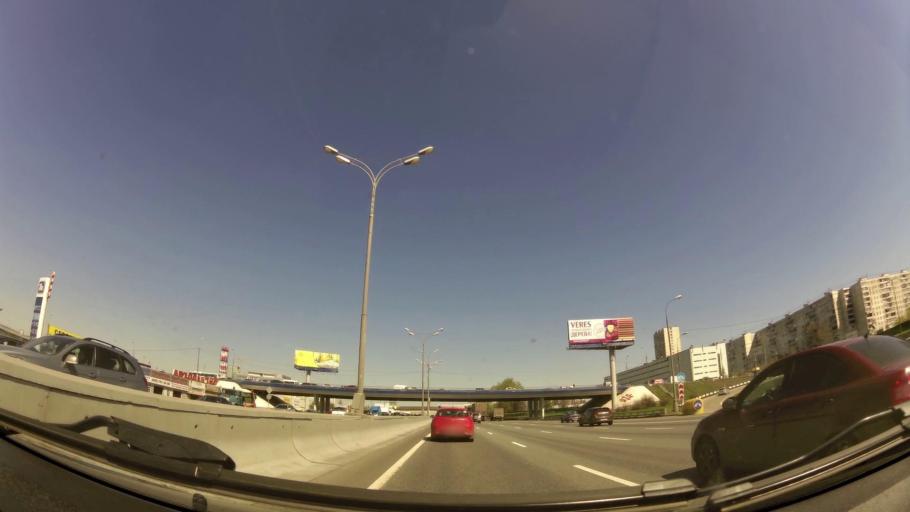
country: RU
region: Moscow
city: Strogino
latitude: 55.8081
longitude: 37.3882
